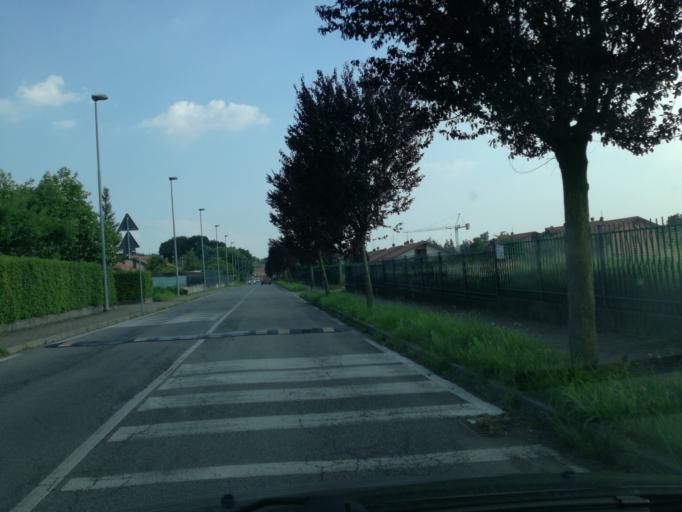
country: IT
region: Lombardy
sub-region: Provincia di Lecco
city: Robbiate
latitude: 45.6836
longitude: 9.4407
